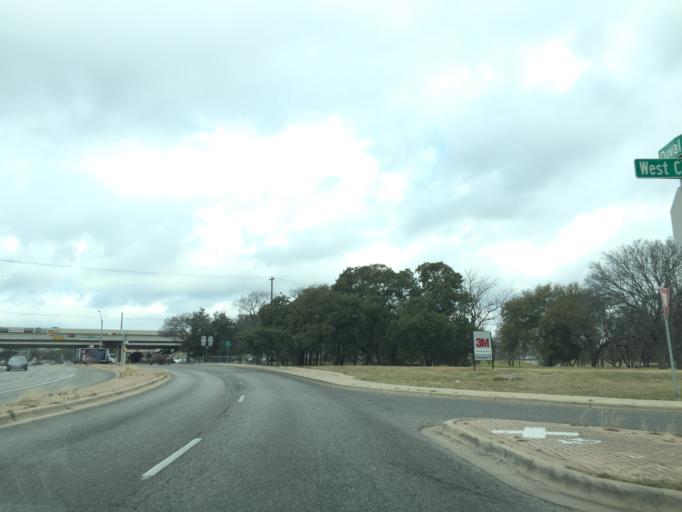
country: US
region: Texas
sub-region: Williamson County
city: Jollyville
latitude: 30.4190
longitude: -97.7451
